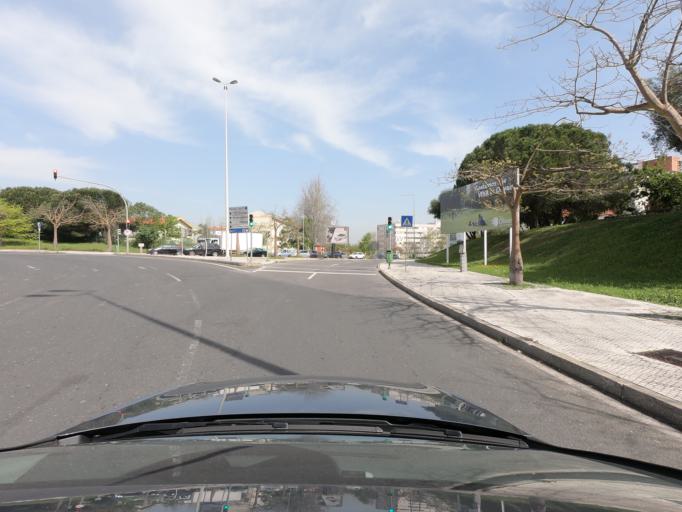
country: PT
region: Lisbon
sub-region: Loures
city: Moscavide
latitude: 38.7613
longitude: -9.1204
